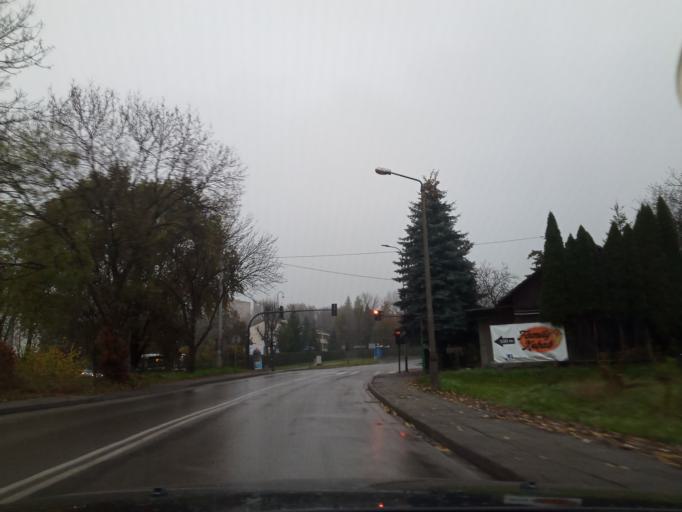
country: PL
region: Lesser Poland Voivodeship
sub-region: Powiat wielicki
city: Kokotow
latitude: 50.0906
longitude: 20.0573
